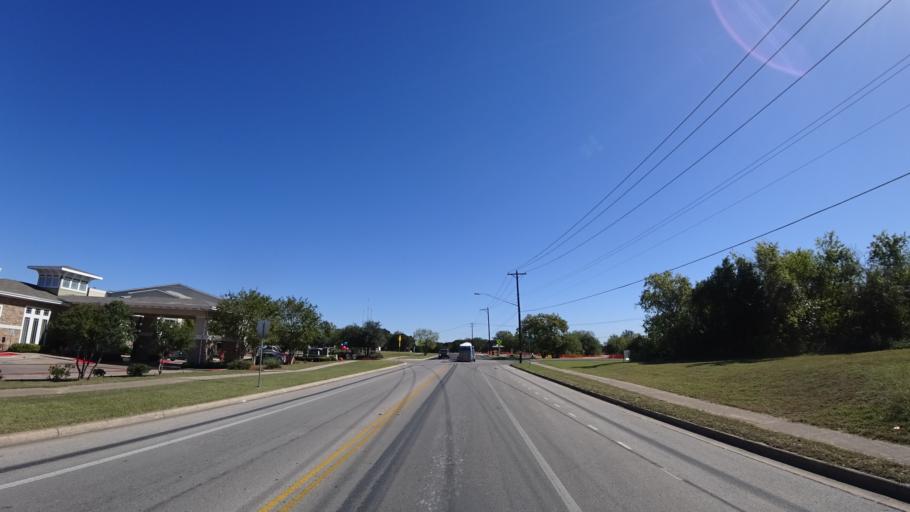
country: US
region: Texas
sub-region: Travis County
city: Austin
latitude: 30.2838
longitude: -97.6722
